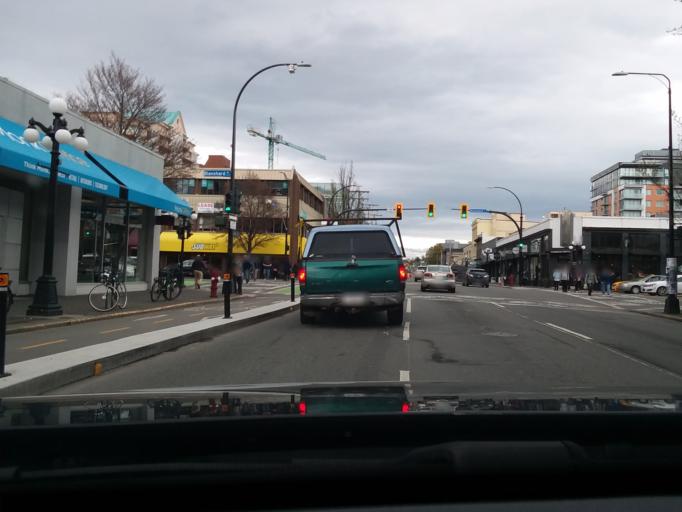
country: CA
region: British Columbia
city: Victoria
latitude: 48.4244
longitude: -123.3631
